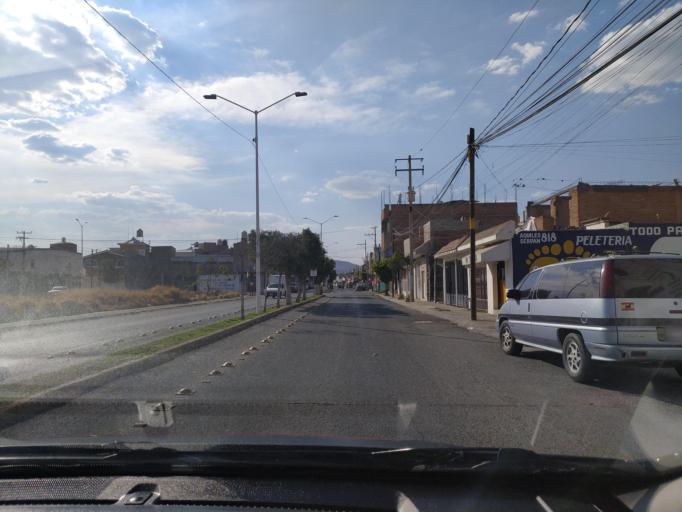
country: MX
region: Guanajuato
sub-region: San Francisco del Rincon
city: Fraccionamiento la Mezquitera
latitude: 21.0135
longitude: -101.8439
